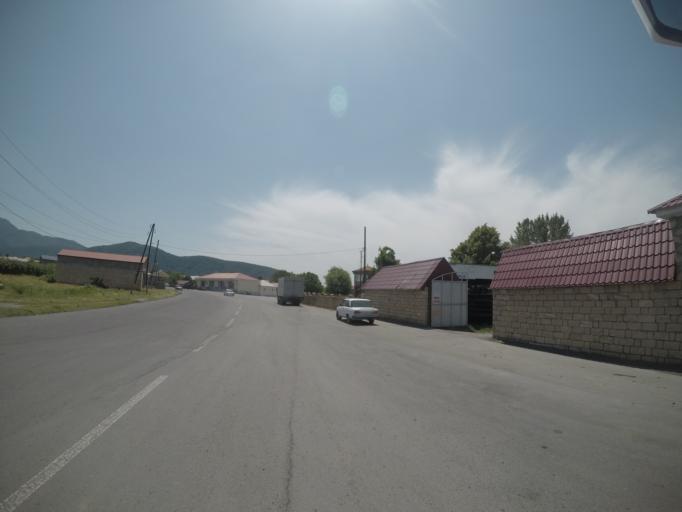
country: AZ
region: Qakh Rayon
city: Qax
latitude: 41.4155
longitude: 46.9071
